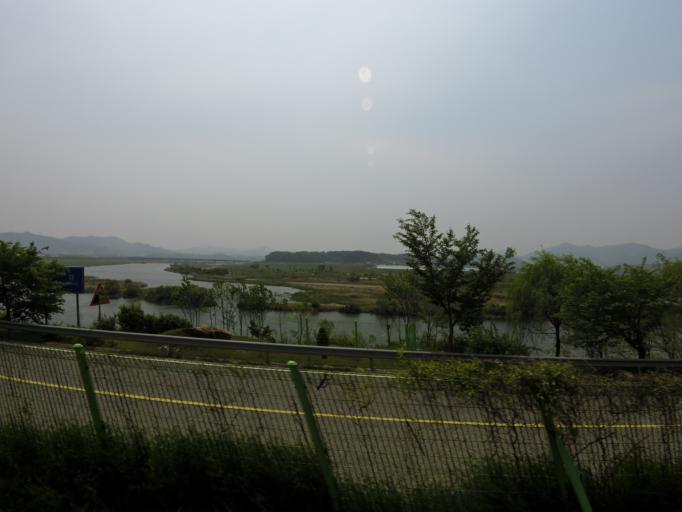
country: KR
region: Chungcheongbuk-do
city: Yong-dong
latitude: 36.2431
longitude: 127.7067
